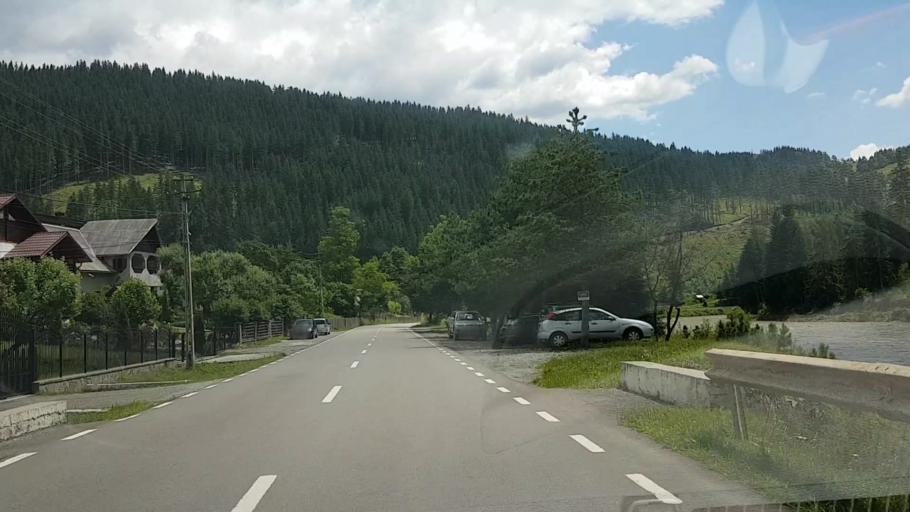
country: RO
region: Suceava
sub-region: Comuna Crucea
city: Crucea
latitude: 47.3570
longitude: 25.6119
